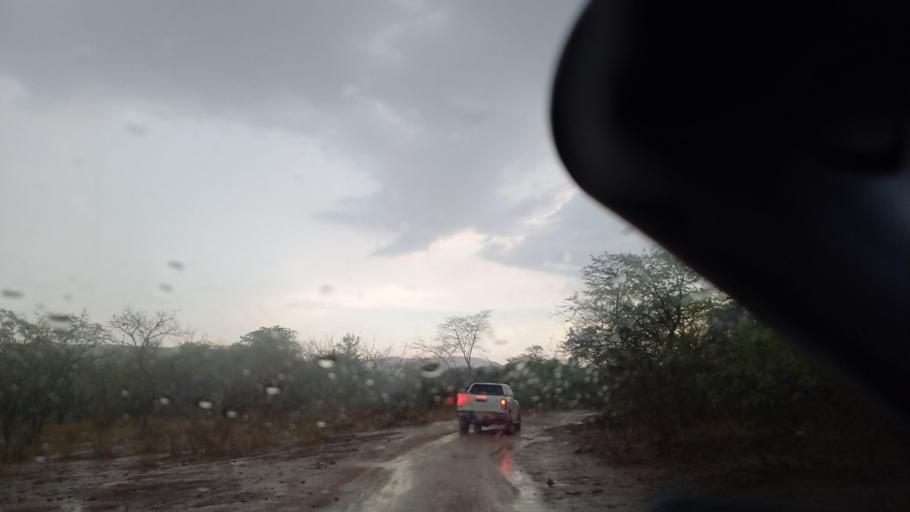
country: ZM
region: Lusaka
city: Kafue
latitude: -15.9476
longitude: 28.2210
